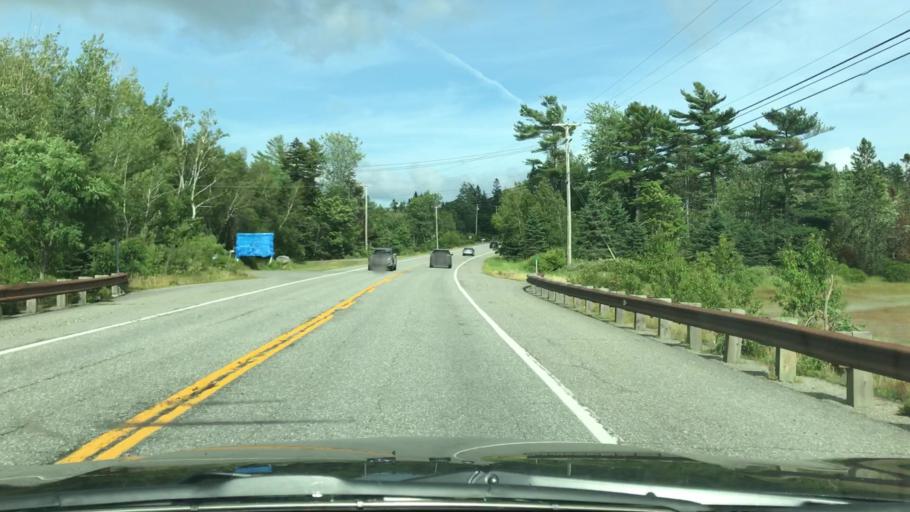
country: US
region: Maine
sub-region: Hancock County
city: Trenton
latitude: 44.4190
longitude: -68.3505
